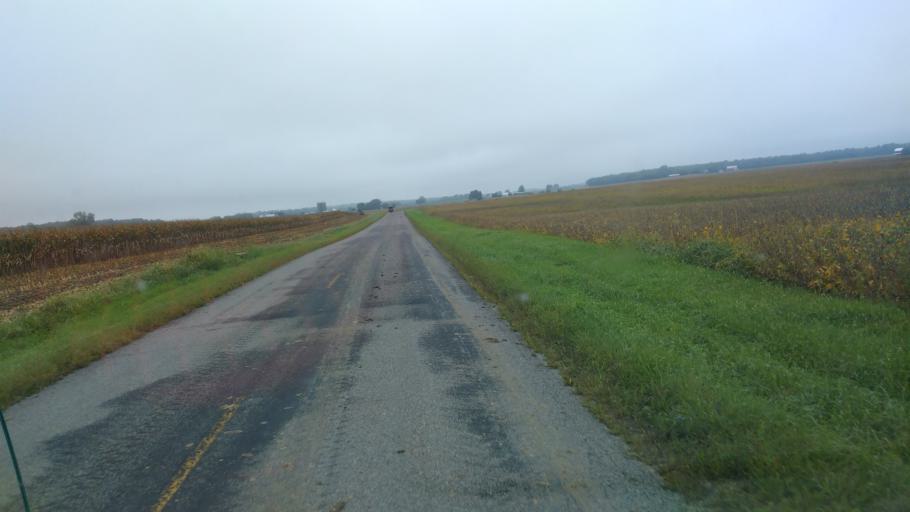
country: US
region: Ohio
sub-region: Hardin County
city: Kenton
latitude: 40.5381
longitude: -83.6323
